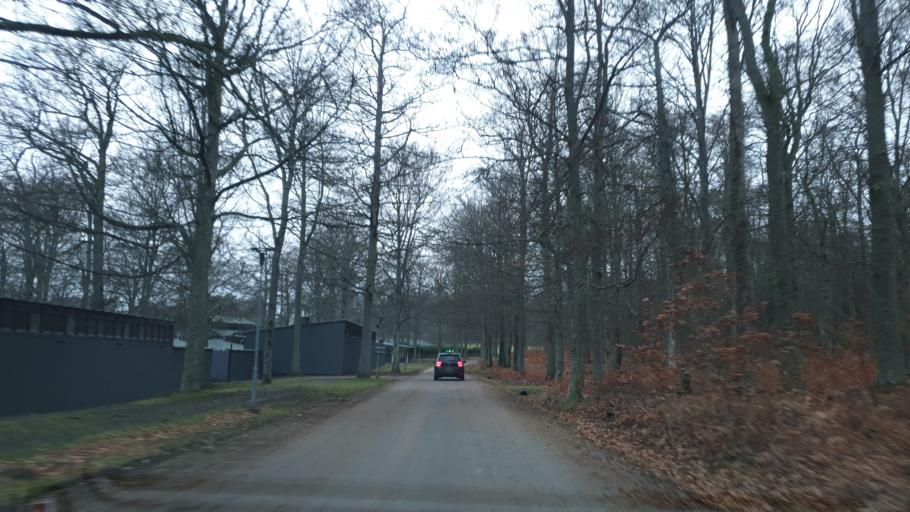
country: SE
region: Blekinge
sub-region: Karlskrona Kommun
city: Rodeby
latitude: 56.2146
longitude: 15.6839
